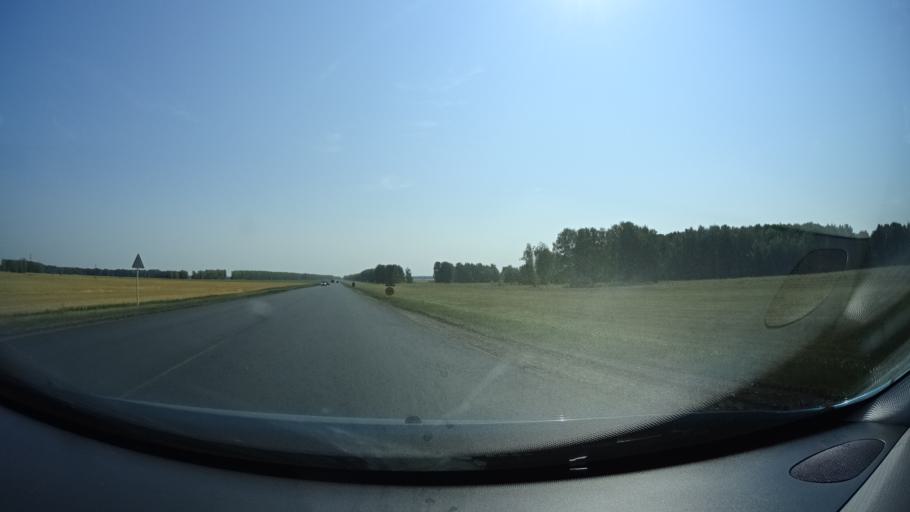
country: RU
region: Bashkortostan
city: Karmaskaly
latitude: 54.4011
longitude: 56.0915
